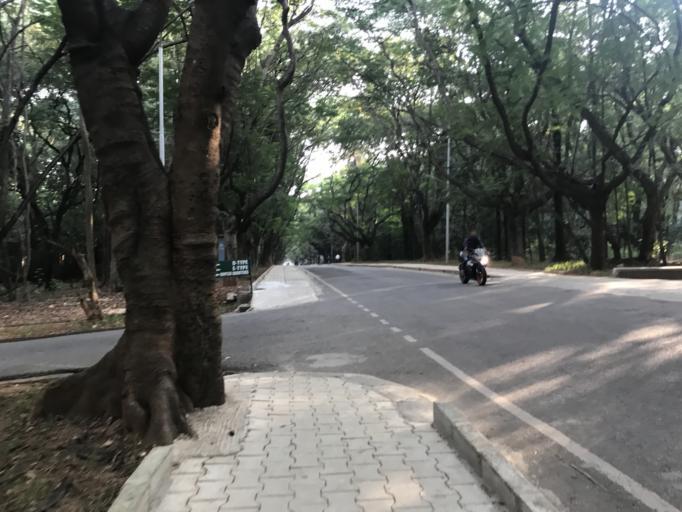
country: IN
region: Karnataka
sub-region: Bangalore Urban
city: Bangalore
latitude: 13.0226
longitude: 77.5667
